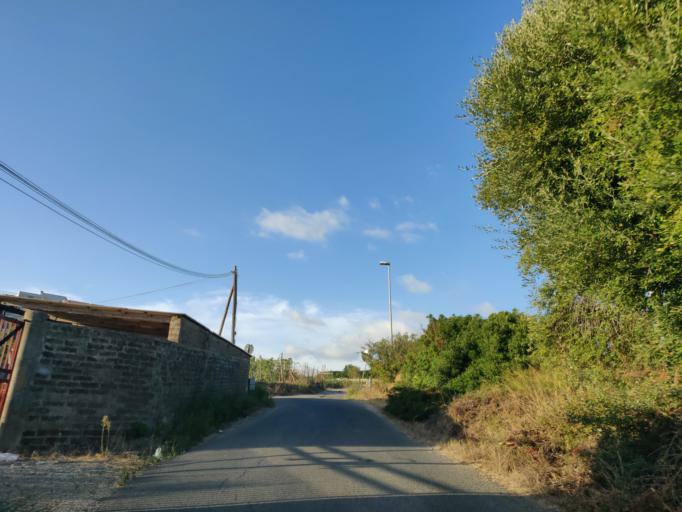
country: IT
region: Latium
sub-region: Citta metropolitana di Roma Capitale
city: Civitavecchia
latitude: 42.0934
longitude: 11.8184
